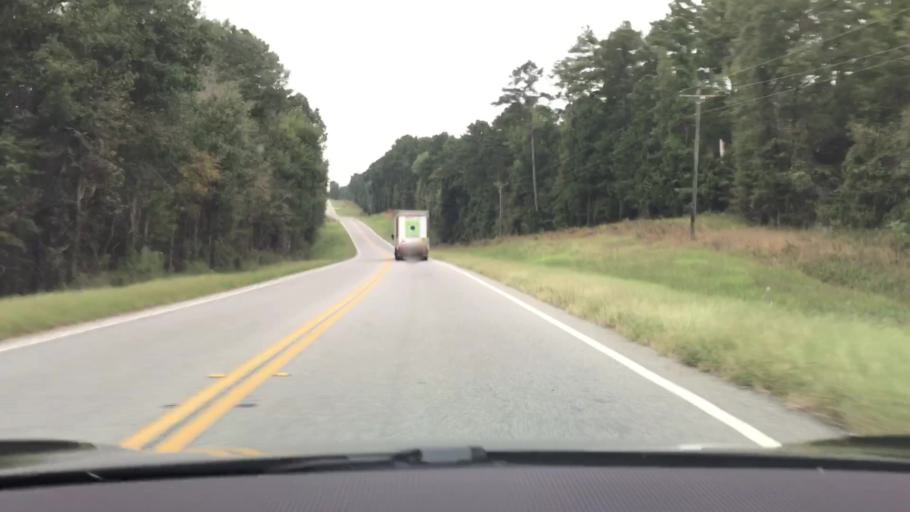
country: US
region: Georgia
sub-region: Greene County
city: Greensboro
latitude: 33.6537
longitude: -83.2369
